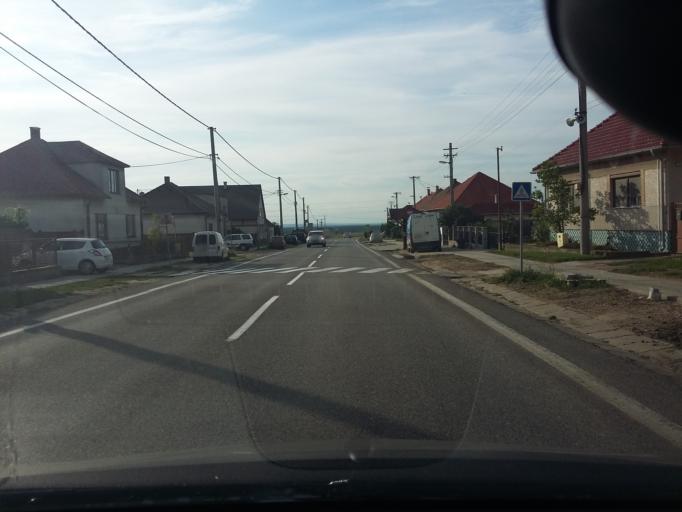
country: SK
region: Bratislavsky
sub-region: Okres Malacky
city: Malacky
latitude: 48.3697
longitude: 17.1380
